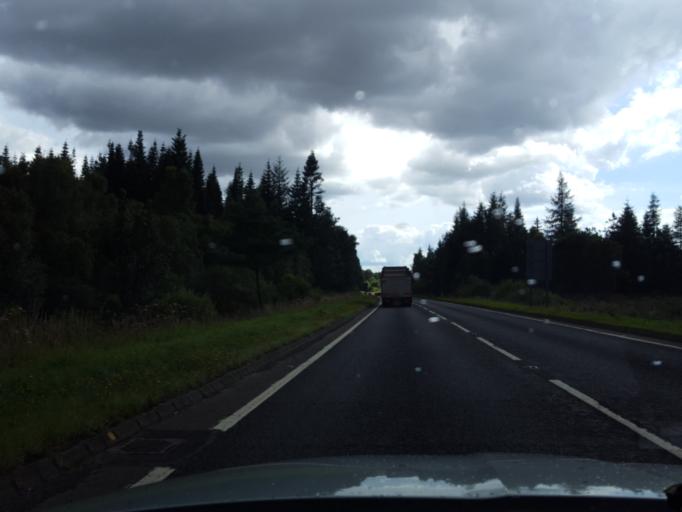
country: GB
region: Scotland
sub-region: Perth and Kinross
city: Bankfoot
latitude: 56.5227
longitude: -3.5176
